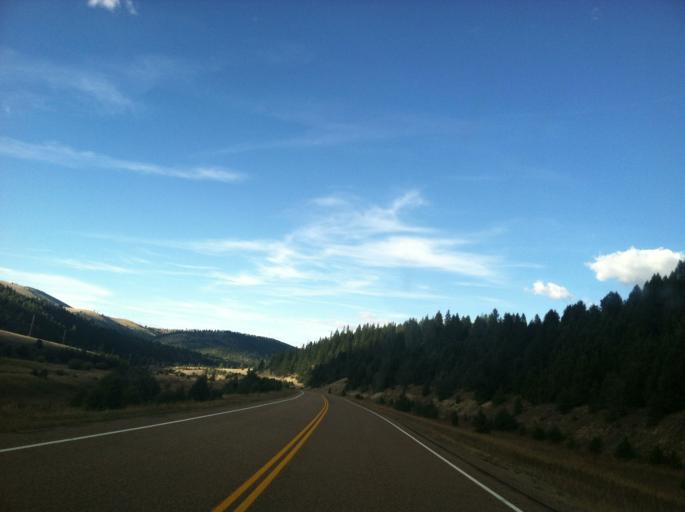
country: US
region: Montana
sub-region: Granite County
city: Philipsburg
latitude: 46.3862
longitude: -113.3102
